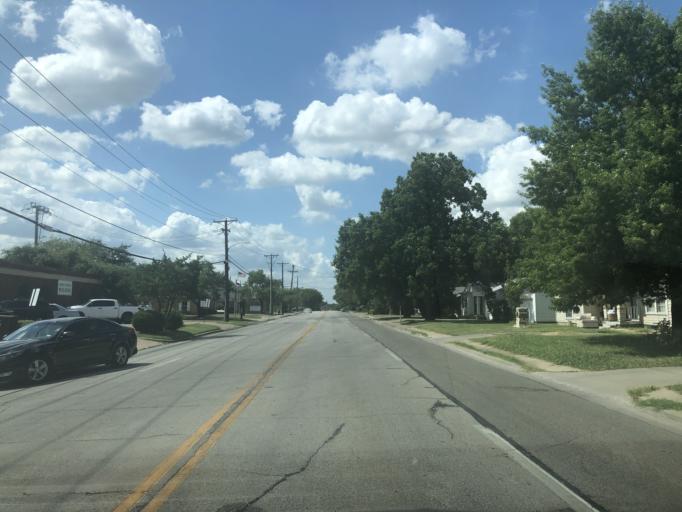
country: US
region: Texas
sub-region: Dallas County
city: Grand Prairie
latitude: 32.7343
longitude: -97.0059
